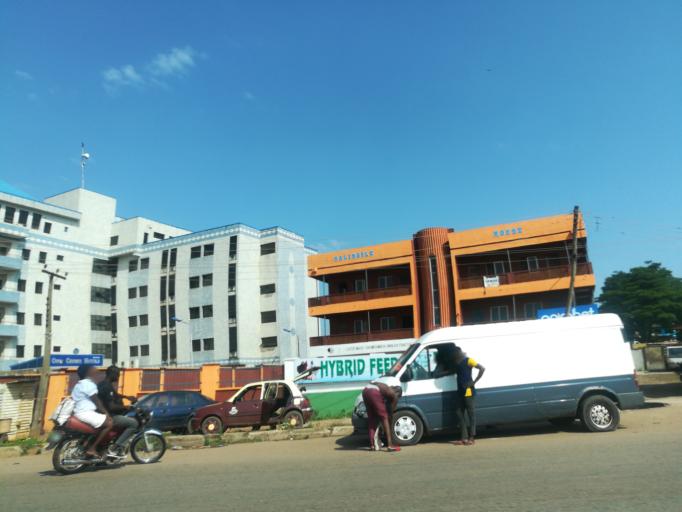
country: NG
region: Oyo
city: Ibadan
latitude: 7.4103
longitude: 3.9504
